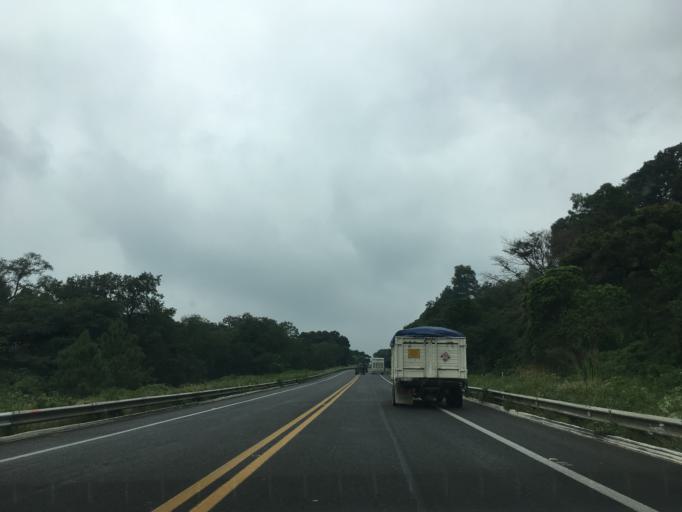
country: MX
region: Michoacan
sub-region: Ziracuaretiro
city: Patuan
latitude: 19.4165
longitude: -101.9488
